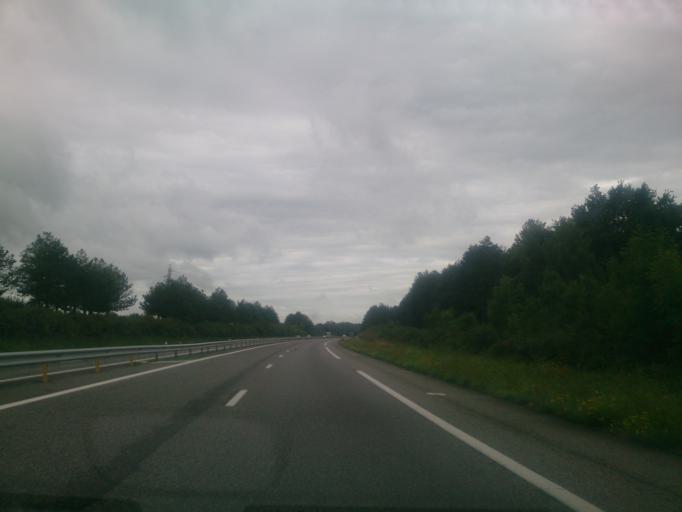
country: FR
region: Midi-Pyrenees
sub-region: Departement de la Haute-Garonne
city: Montrejeau
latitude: 43.0908
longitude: 0.5227
